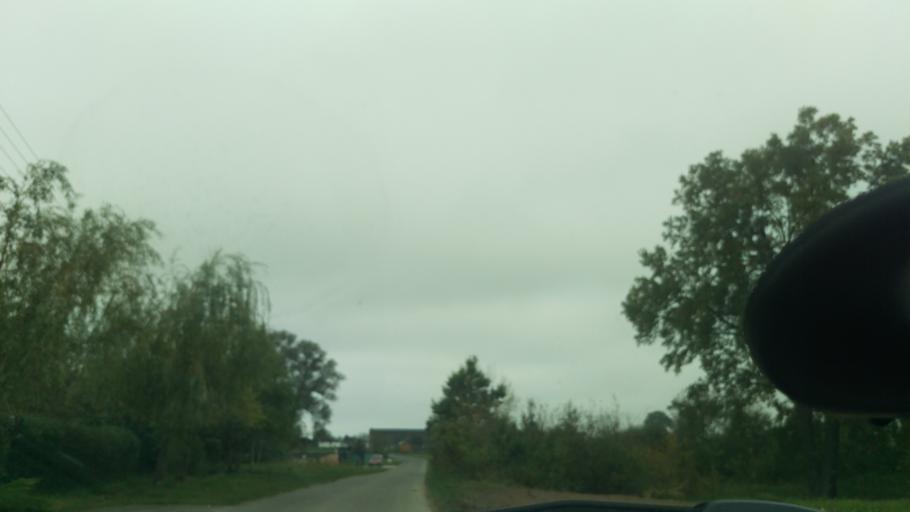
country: PL
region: West Pomeranian Voivodeship
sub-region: Powiat pyrzycki
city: Przelewice
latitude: 53.0430
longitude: 15.1412
